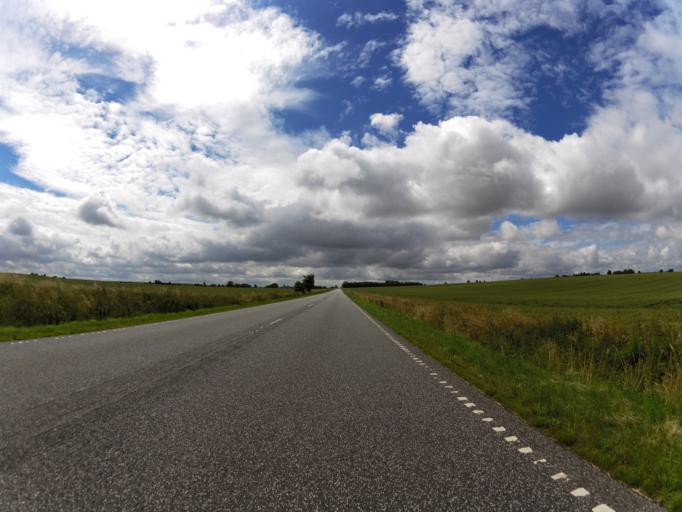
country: DK
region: North Denmark
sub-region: Mariagerfjord Kommune
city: Hadsund
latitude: 56.6194
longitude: 10.1542
